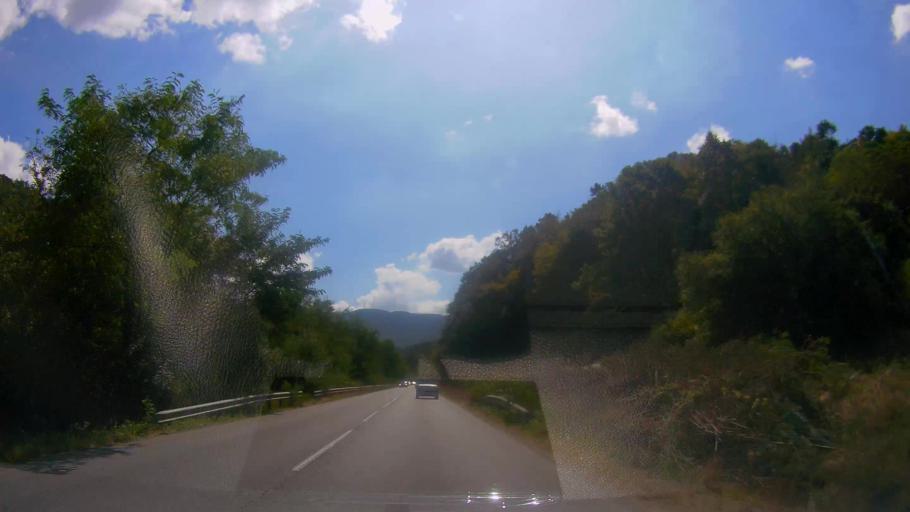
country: BG
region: Stara Zagora
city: Gurkovo
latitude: 42.7307
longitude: 25.7120
